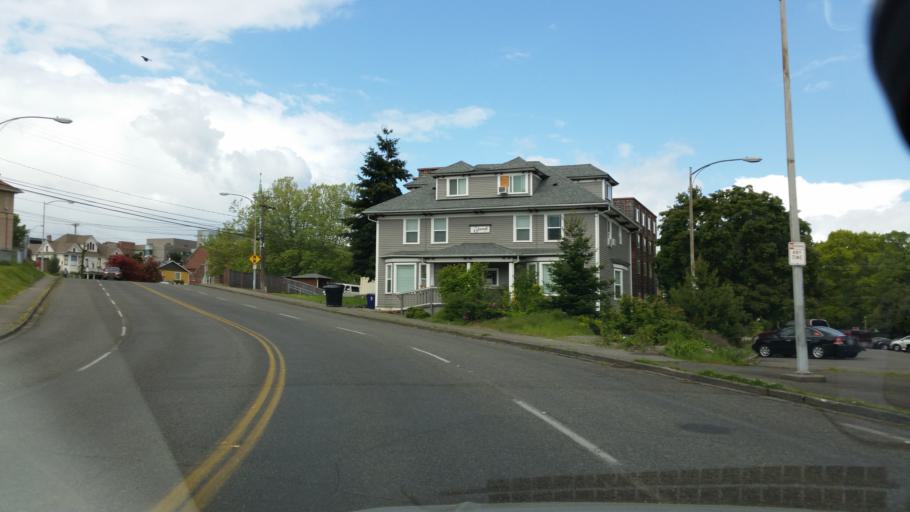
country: US
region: Washington
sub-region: Pierce County
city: Tacoma
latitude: 47.2562
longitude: -122.4483
